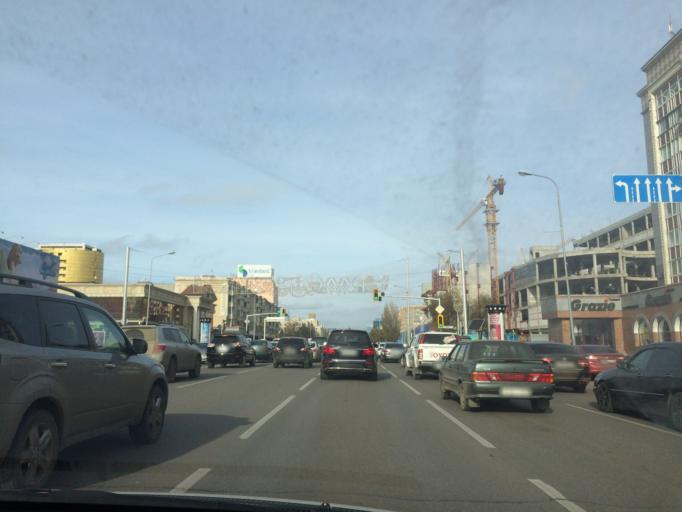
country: KZ
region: Astana Qalasy
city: Astana
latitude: 51.1621
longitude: 71.4285
